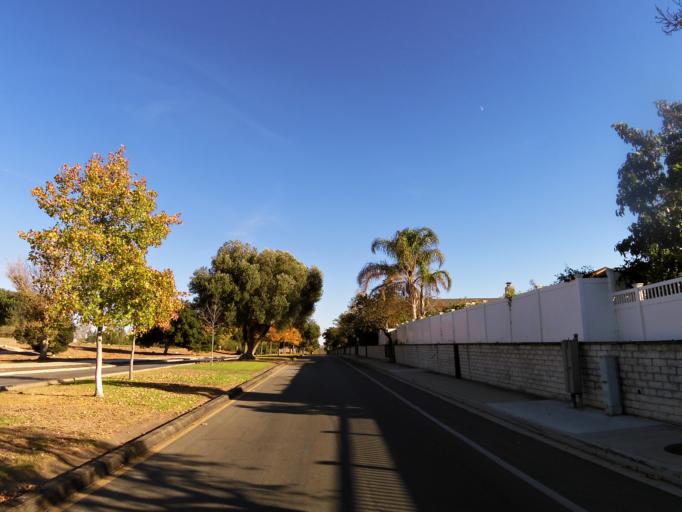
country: US
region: California
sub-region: Ventura County
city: Casa Conejo
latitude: 34.2183
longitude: -118.8973
